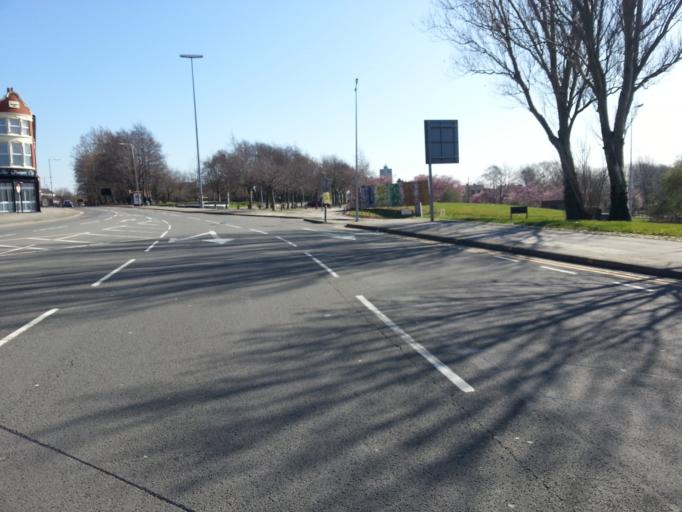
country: GB
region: England
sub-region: Liverpool
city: Liverpool
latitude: 53.3941
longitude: -2.9756
